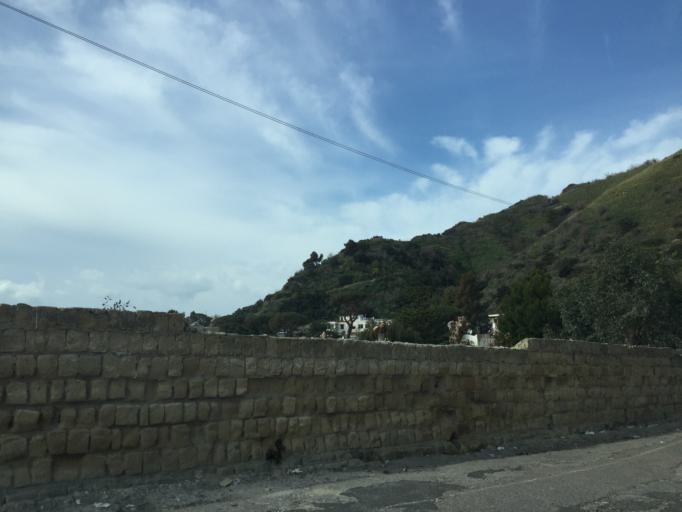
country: IT
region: Campania
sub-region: Provincia di Napoli
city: Bacoli
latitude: 40.7793
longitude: 14.0896
